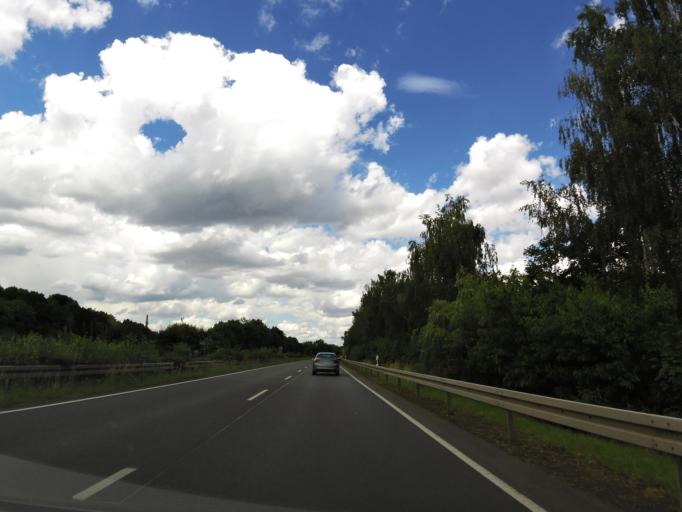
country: DE
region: Saxony
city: Markkleeberg
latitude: 51.2626
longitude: 12.3826
